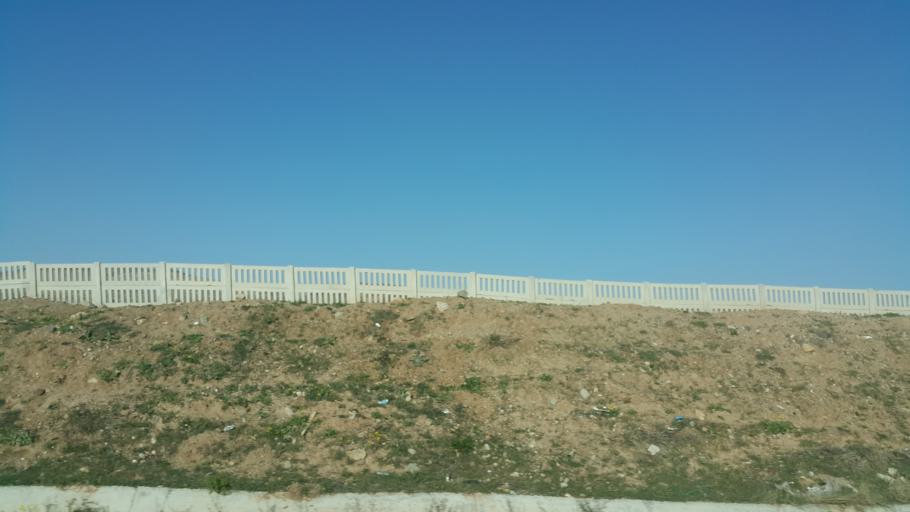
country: TR
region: Aksaray
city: Acipinar
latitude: 38.7177
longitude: 33.6754
